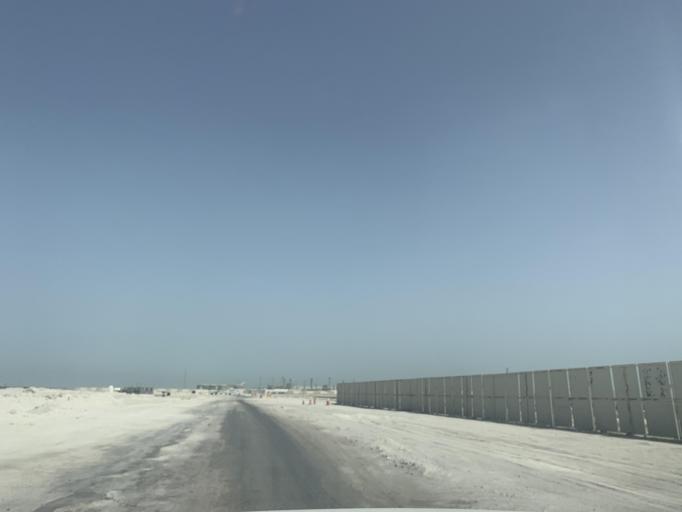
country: BH
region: Northern
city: Sitrah
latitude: 26.1568
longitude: 50.6316
